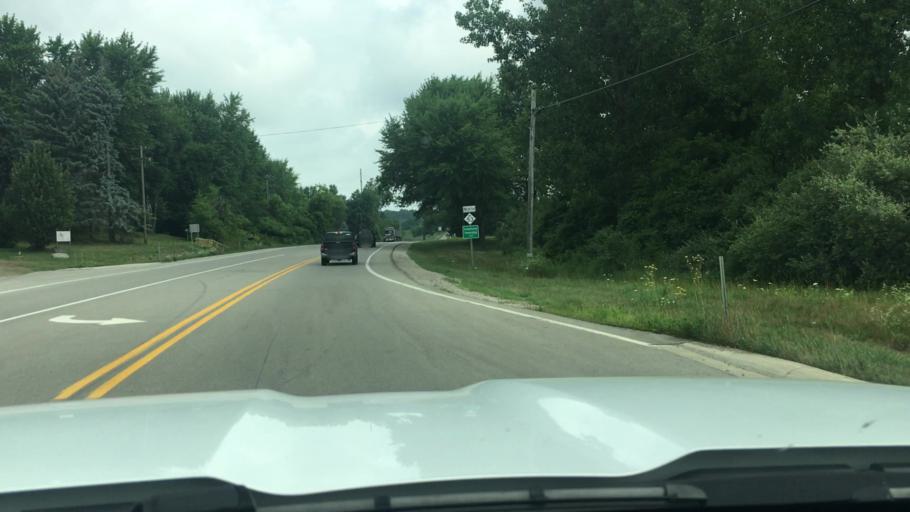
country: US
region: Michigan
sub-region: Lapeer County
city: Imlay City
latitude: 43.0657
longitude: -83.0744
